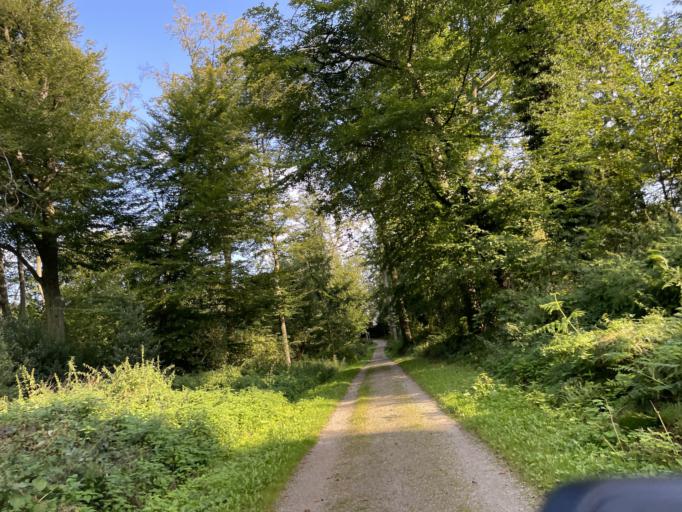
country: DE
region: North Rhine-Westphalia
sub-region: Regierungsbezirk Dusseldorf
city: Essen
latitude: 51.4131
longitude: 7.0514
